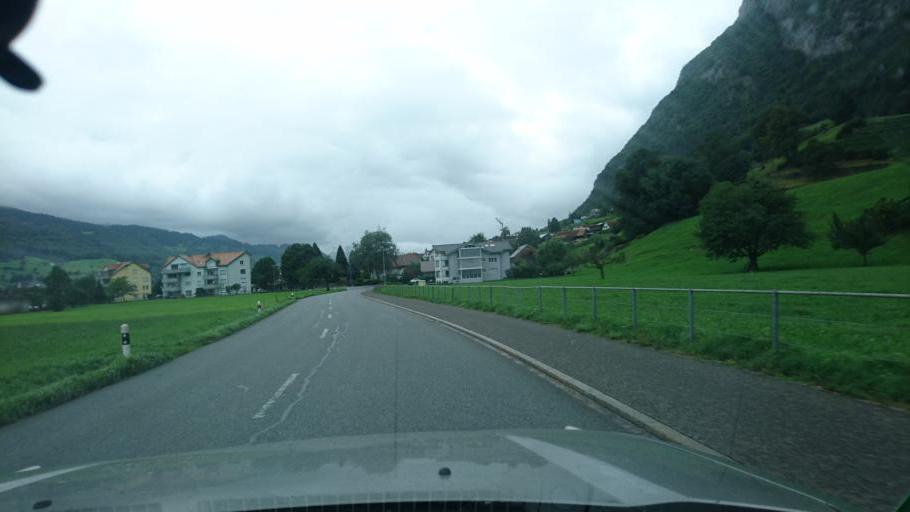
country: CH
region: Saint Gallen
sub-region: Wahlkreis Sarganserland
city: Sargans
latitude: 47.0549
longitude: 9.4225
